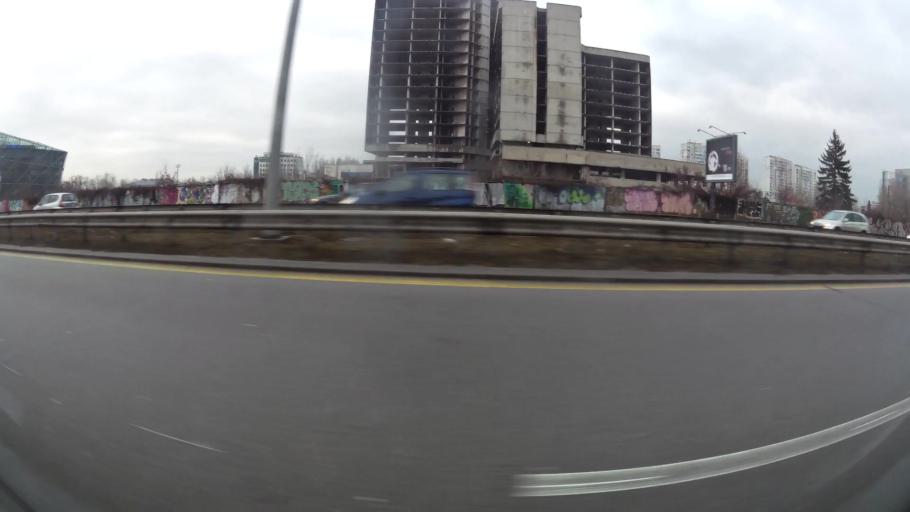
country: BG
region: Sofia-Capital
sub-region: Stolichna Obshtina
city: Sofia
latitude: 42.6635
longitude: 23.3753
